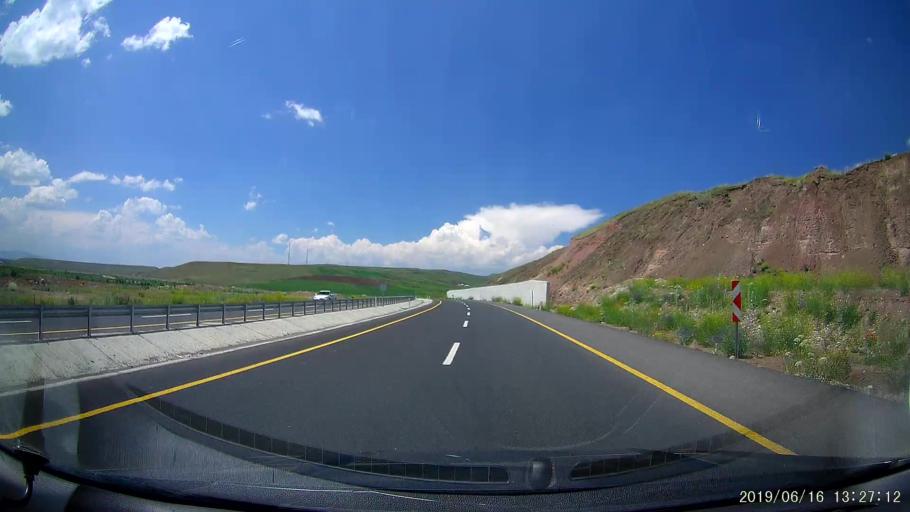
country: TR
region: Agri
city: Taslicay
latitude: 39.6686
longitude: 43.3151
